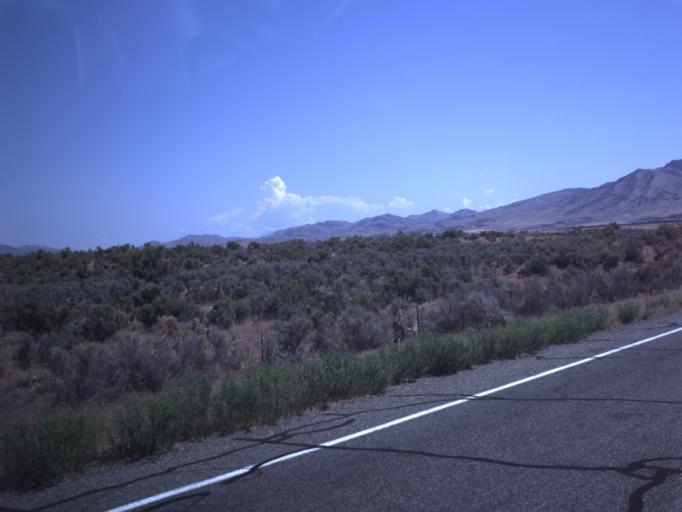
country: US
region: Utah
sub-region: Millard County
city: Delta
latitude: 39.3543
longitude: -112.4180
